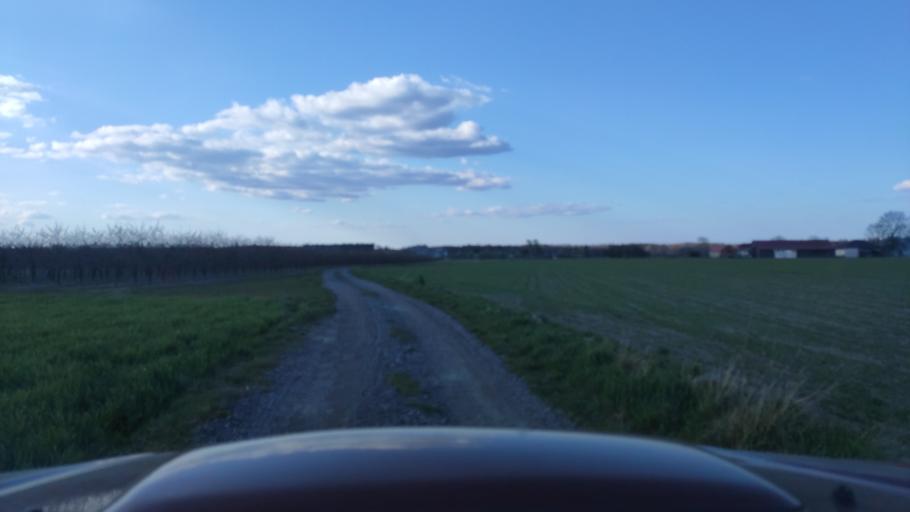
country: PL
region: Masovian Voivodeship
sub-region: Powiat zwolenski
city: Zwolen
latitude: 51.3770
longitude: 21.5755
